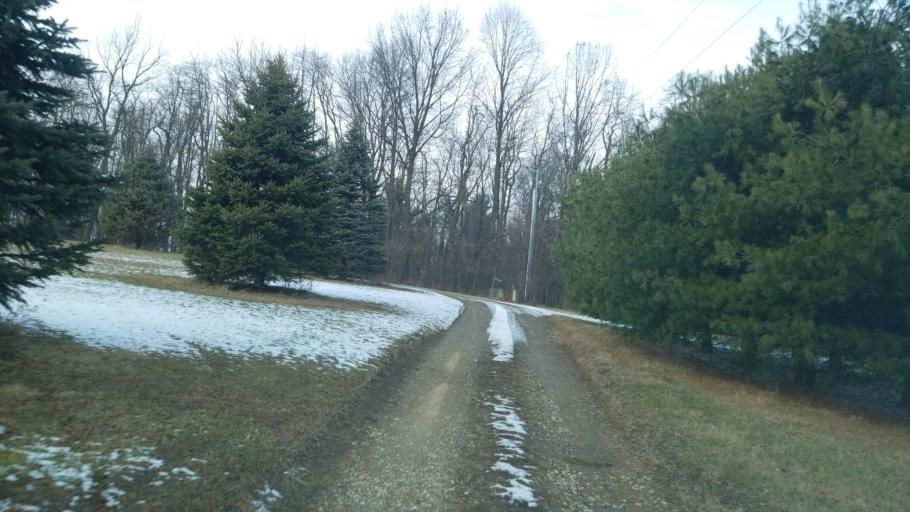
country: US
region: Ohio
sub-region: Sandusky County
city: Bellville
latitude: 40.5901
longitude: -82.5551
